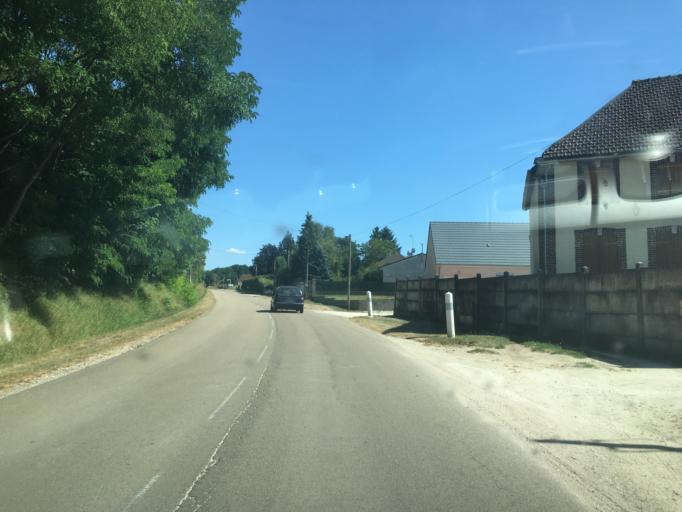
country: FR
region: Bourgogne
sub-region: Departement de l'Yonne
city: Fleury-la-Vallee
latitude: 47.8593
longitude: 3.4470
